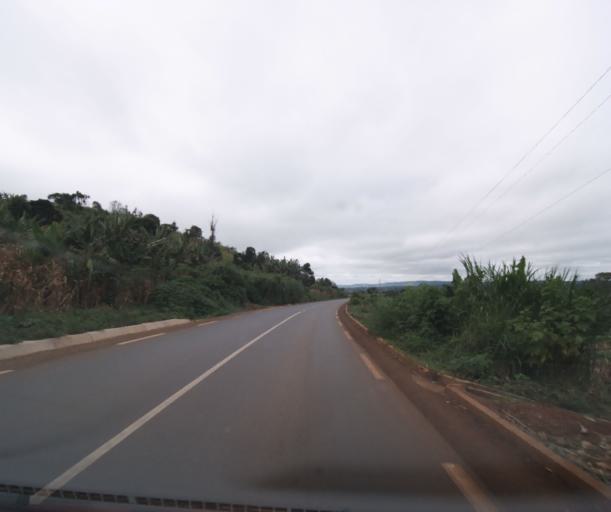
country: CM
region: West
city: Bansoa
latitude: 5.5498
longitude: 10.3274
